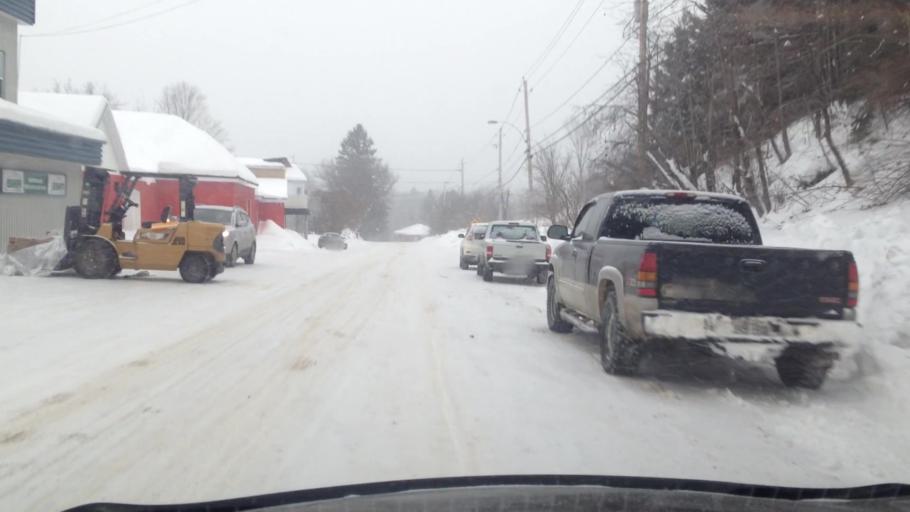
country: CA
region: Quebec
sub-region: Laurentides
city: Mont-Tremblant
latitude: 45.9729
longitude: -74.6354
